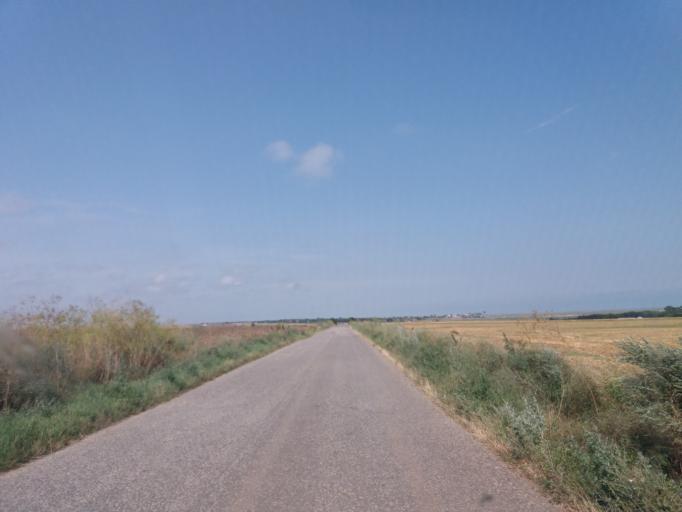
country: RO
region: Constanta
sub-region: Comuna Corbu
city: Corbu
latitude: 44.4276
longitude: 28.7145
